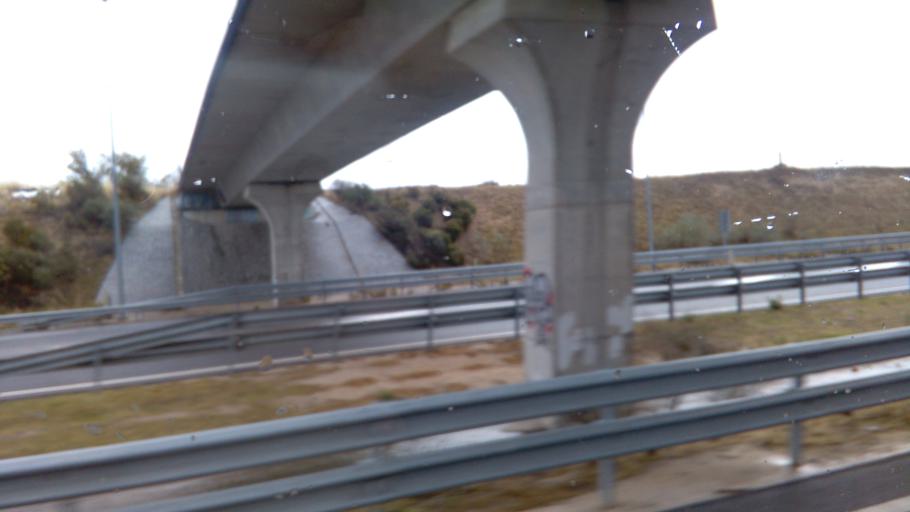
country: ES
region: Madrid
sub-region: Provincia de Madrid
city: Alcorcon
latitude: 40.3271
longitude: -3.8163
